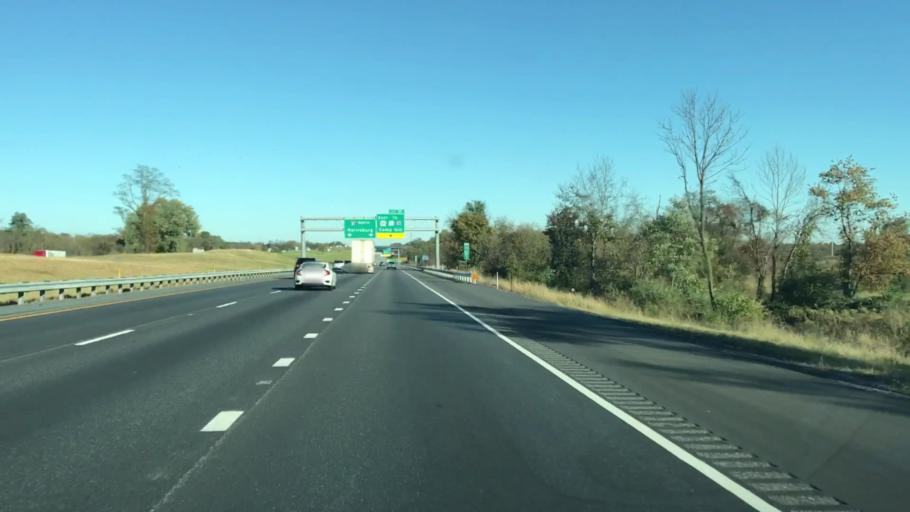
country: US
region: Pennsylvania
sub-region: Cumberland County
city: Mechanicsburg
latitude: 40.2730
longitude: -77.0149
